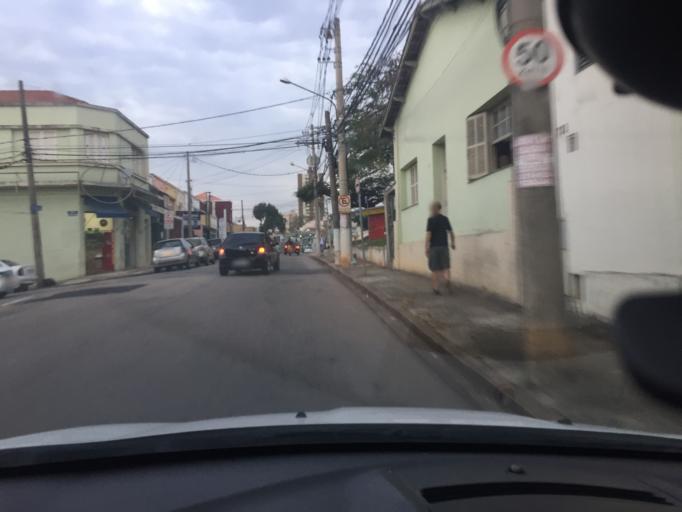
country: BR
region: Sao Paulo
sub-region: Jundiai
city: Jundiai
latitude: -23.1988
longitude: -46.8863
